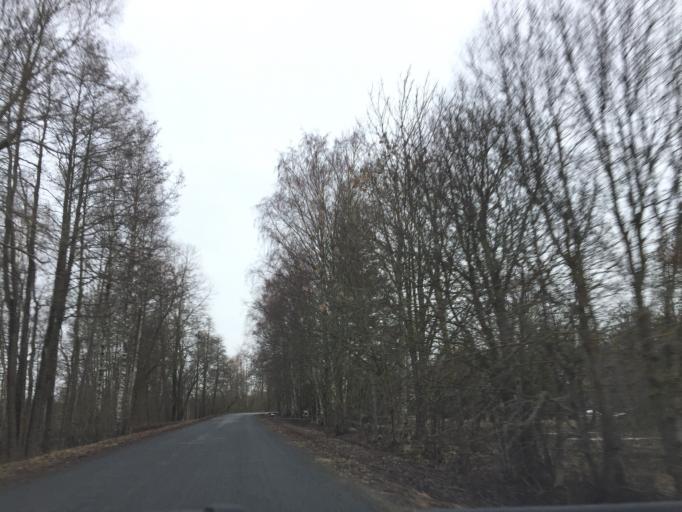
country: EE
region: Laeaene
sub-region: Haapsalu linn
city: Haapsalu
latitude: 58.7821
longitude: 23.4744
